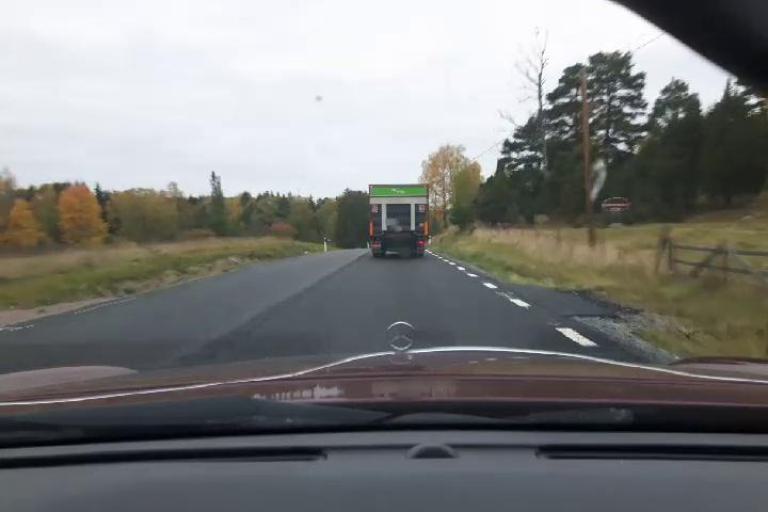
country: SE
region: Soedermanland
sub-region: Strangnas Kommun
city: Strangnas
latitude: 59.4324
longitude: 17.0235
